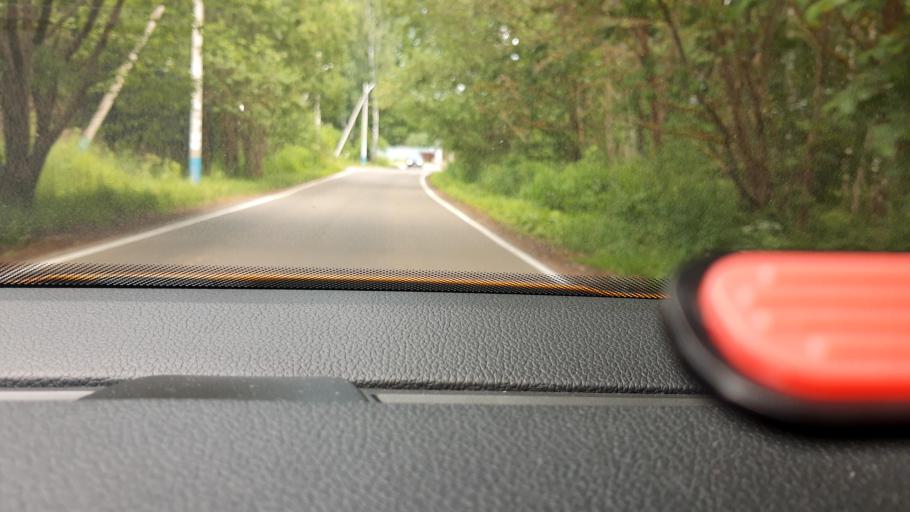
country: RU
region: Moskovskaya
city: Firsanovka
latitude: 55.9062
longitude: 37.2209
